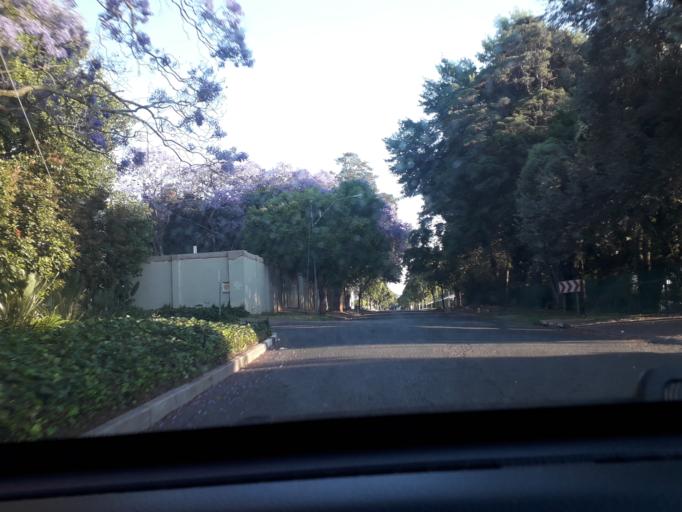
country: ZA
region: Gauteng
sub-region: City of Johannesburg Metropolitan Municipality
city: Johannesburg
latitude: -26.1521
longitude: 28.0537
